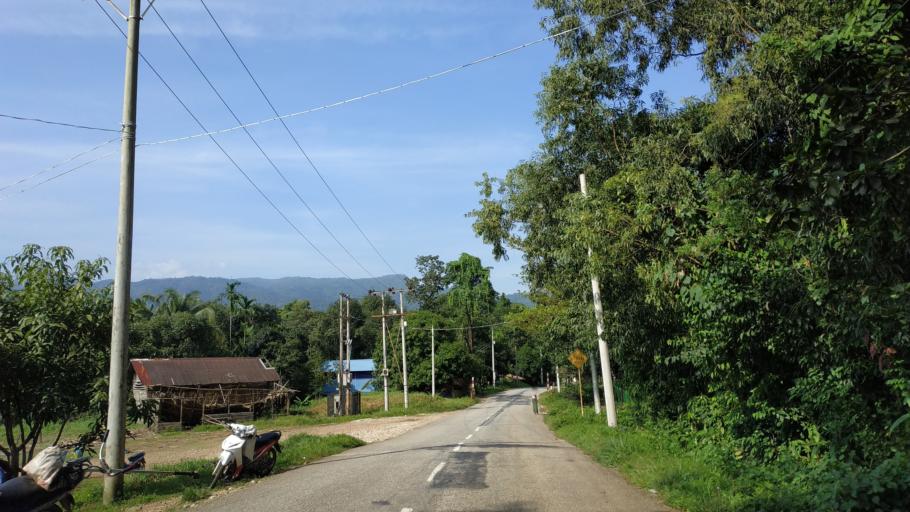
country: MM
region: Tanintharyi
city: Dawei
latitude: 14.5959
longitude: 98.0783
